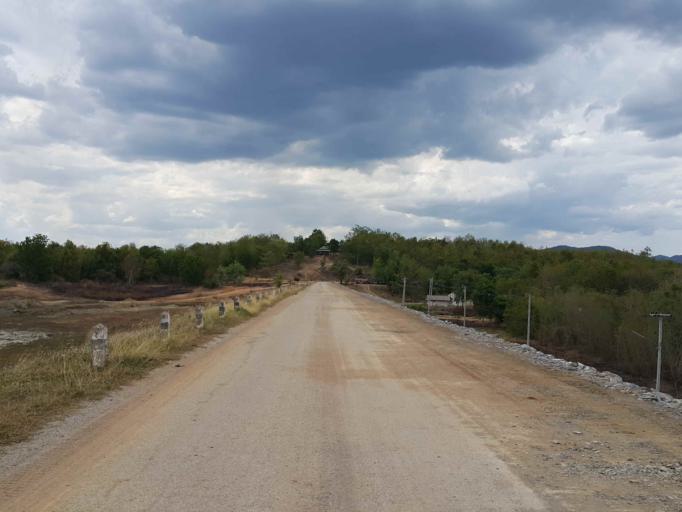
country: TH
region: Sukhothai
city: Thung Saliam
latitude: 17.3247
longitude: 99.4224
